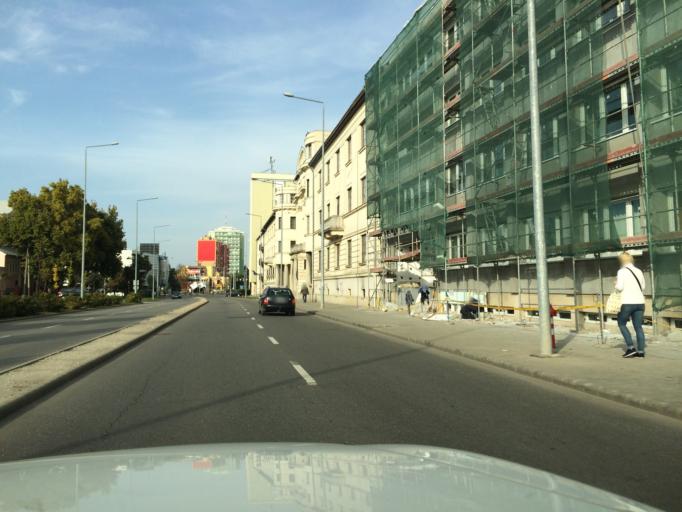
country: HU
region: Szabolcs-Szatmar-Bereg
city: Nyiregyhaza
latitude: 47.9564
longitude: 21.7132
